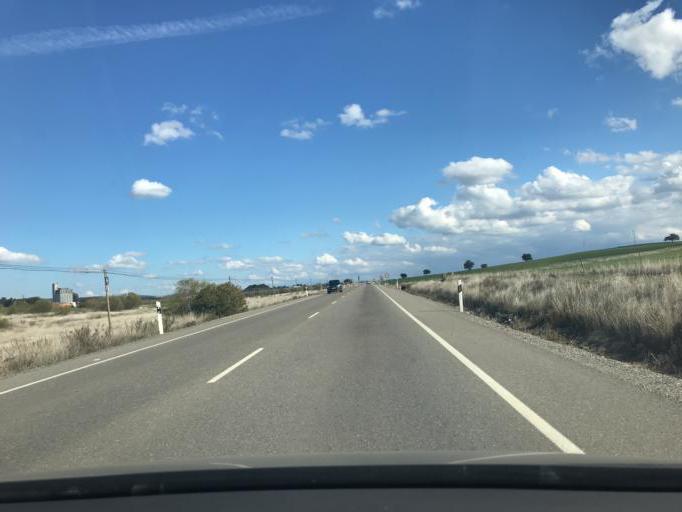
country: ES
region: Andalusia
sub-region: Province of Cordoba
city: Penarroya-Pueblonuevo
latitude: 38.2977
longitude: -5.2991
